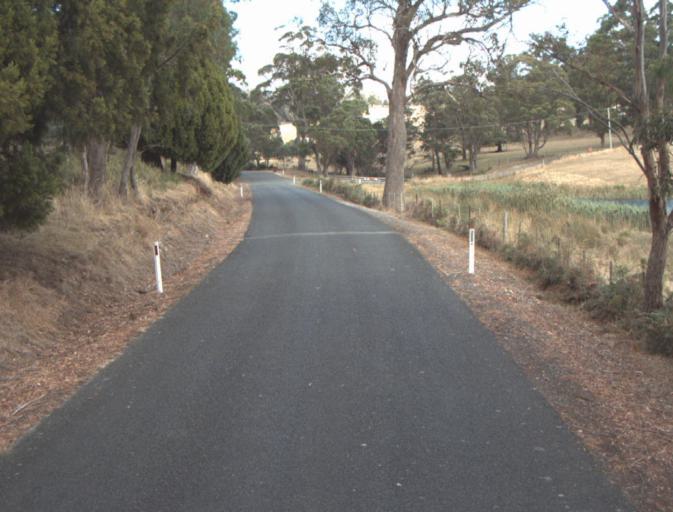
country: AU
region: Tasmania
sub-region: Launceston
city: Mayfield
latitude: -41.2964
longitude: 147.0299
